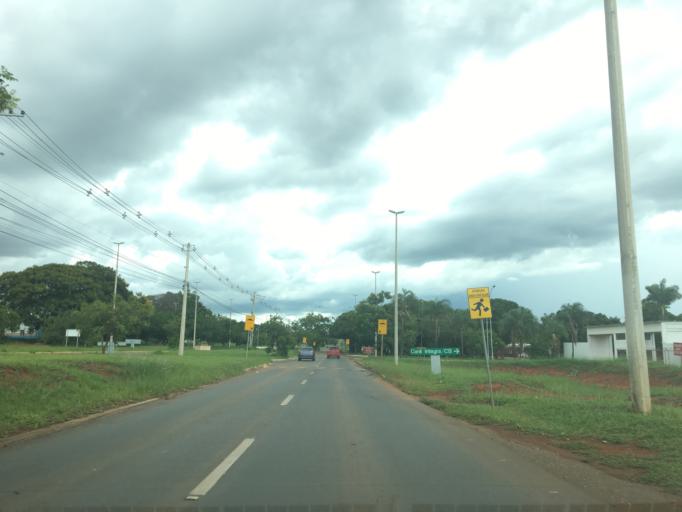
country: BR
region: Federal District
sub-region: Brasilia
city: Brasilia
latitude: -15.8309
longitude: -47.9390
